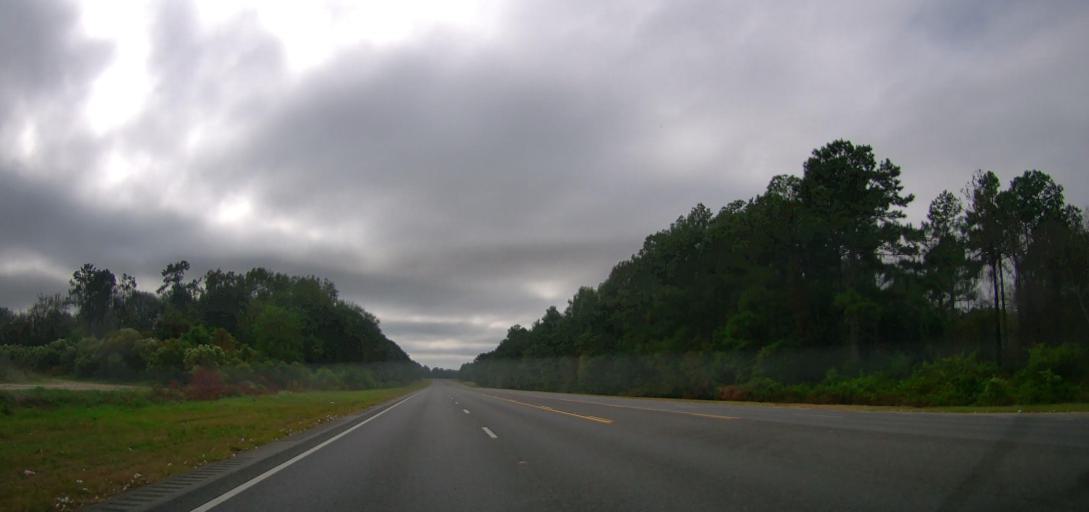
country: US
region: Georgia
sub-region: Colquitt County
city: Moultrie
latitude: 31.0534
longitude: -83.8357
